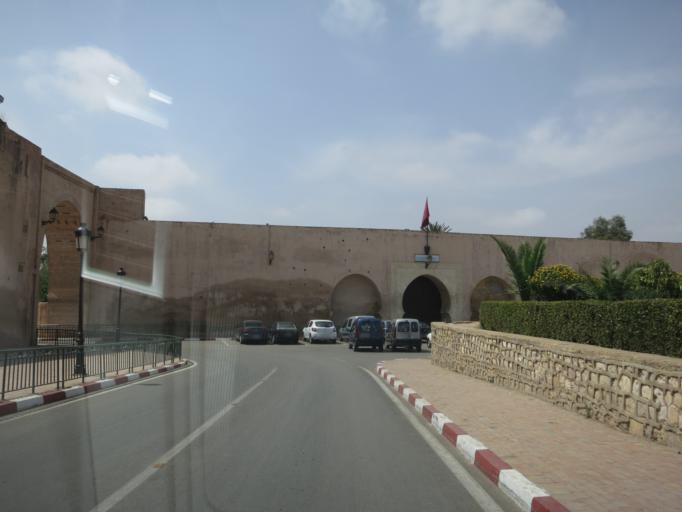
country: MA
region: Meknes-Tafilalet
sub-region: Meknes
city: Meknes
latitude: 33.8922
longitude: -5.5637
